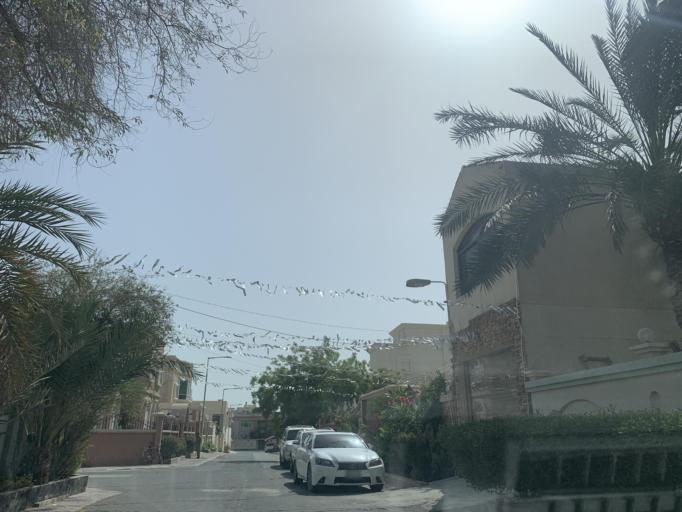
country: BH
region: Northern
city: Ar Rifa'
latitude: 26.1488
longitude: 50.5768
